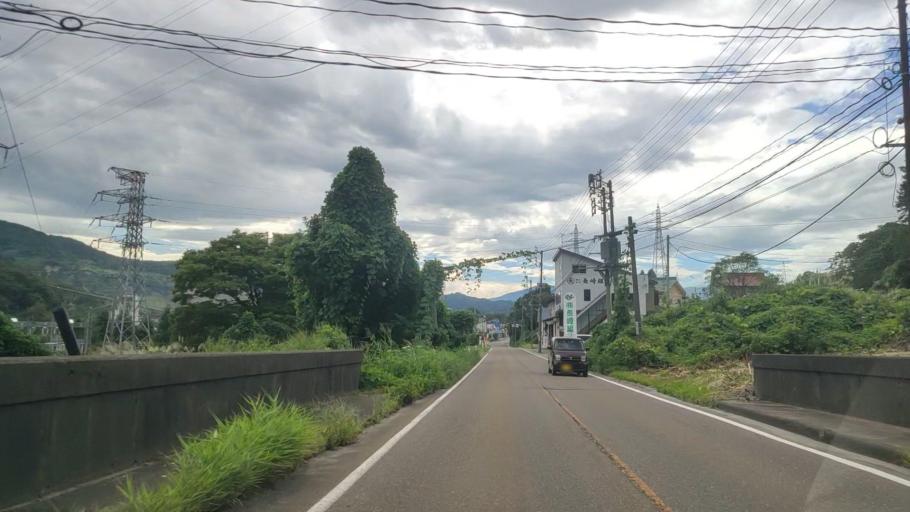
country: JP
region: Niigata
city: Arai
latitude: 36.9946
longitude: 138.2690
